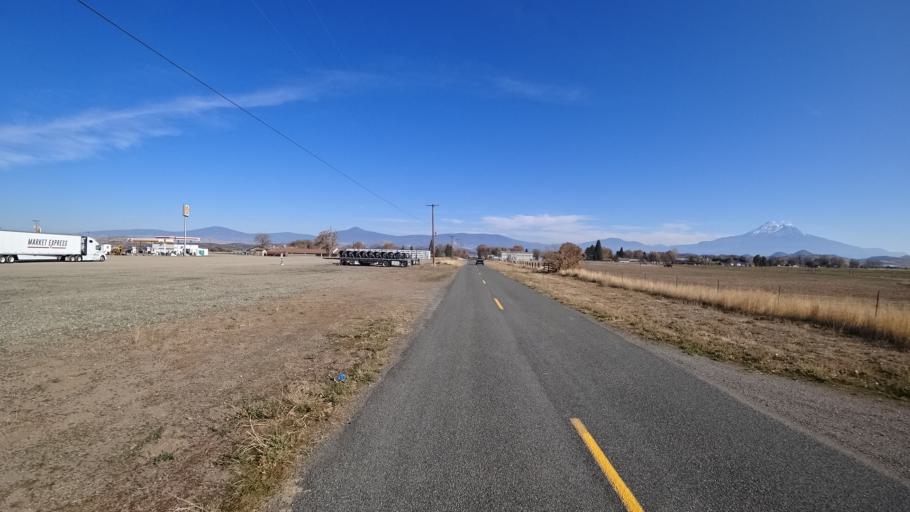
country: US
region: California
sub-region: Siskiyou County
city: Montague
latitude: 41.6456
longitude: -122.5298
